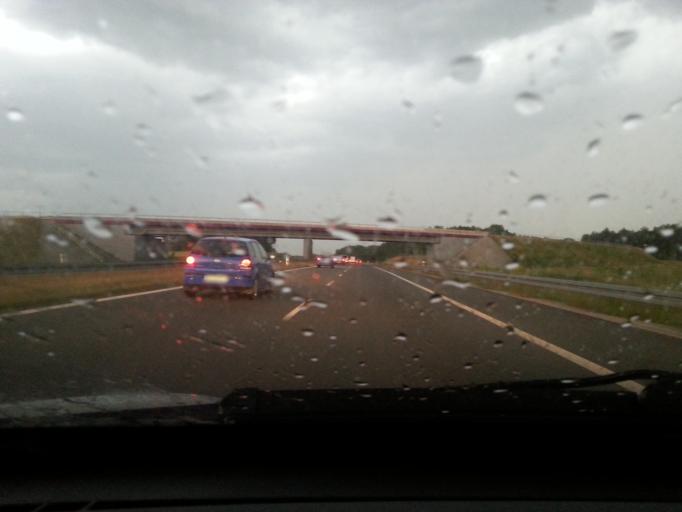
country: PL
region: Lodz Voivodeship
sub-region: powiat Lowicki
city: Lyszkowice
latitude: 51.9659
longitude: 19.8596
